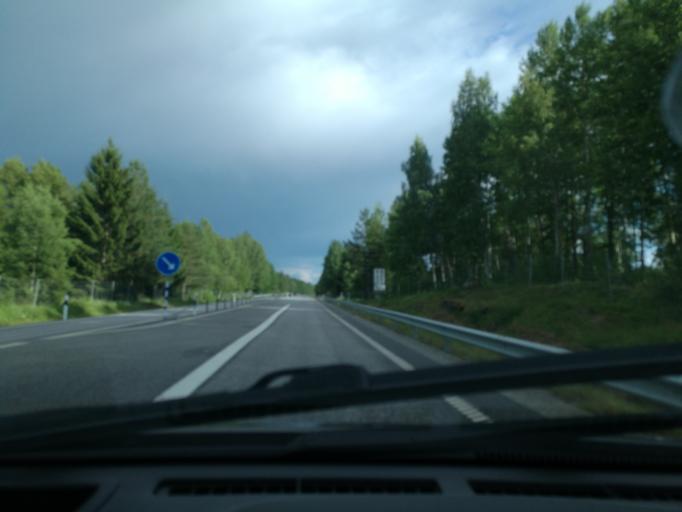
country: SE
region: Vaestmanland
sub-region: Surahammars Kommun
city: Surahammar
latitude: 59.7187
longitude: 16.2392
